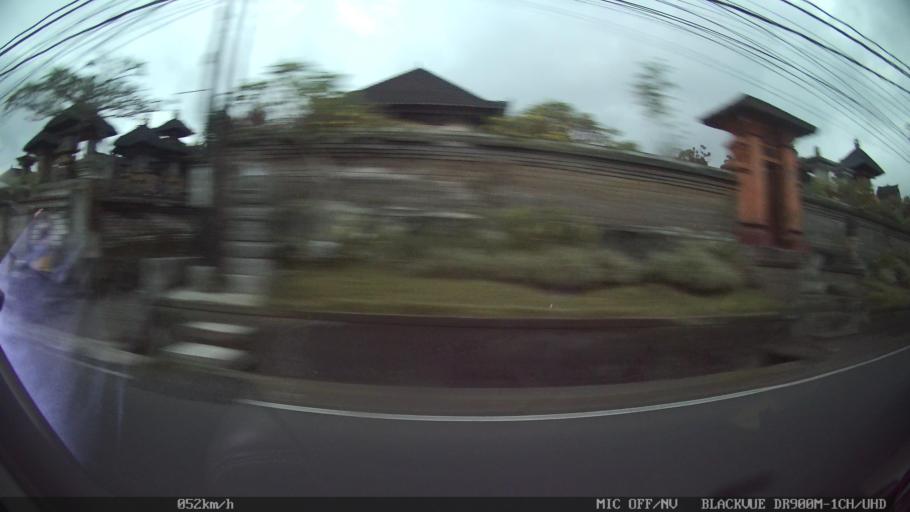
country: ID
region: Bali
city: Bayad
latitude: -8.4474
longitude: 115.2421
